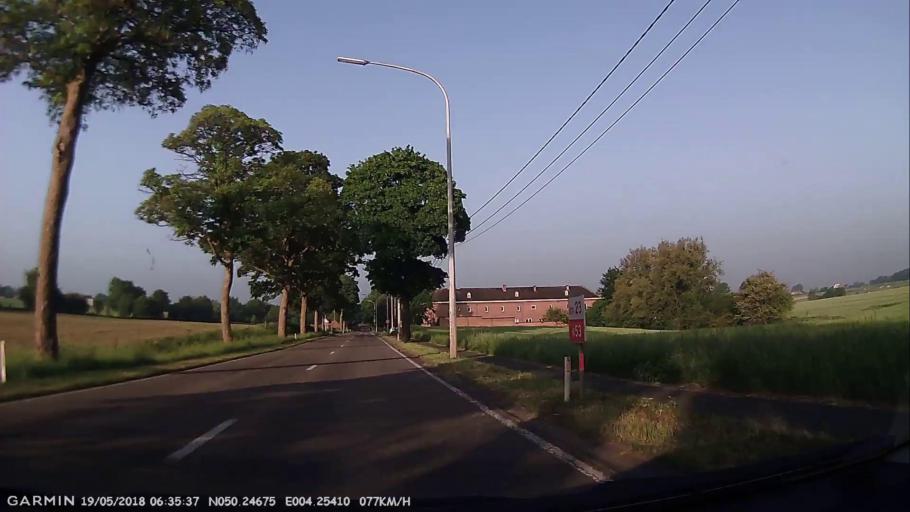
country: BE
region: Wallonia
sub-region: Province du Hainaut
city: Beaumont
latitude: 50.2467
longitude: 4.2540
